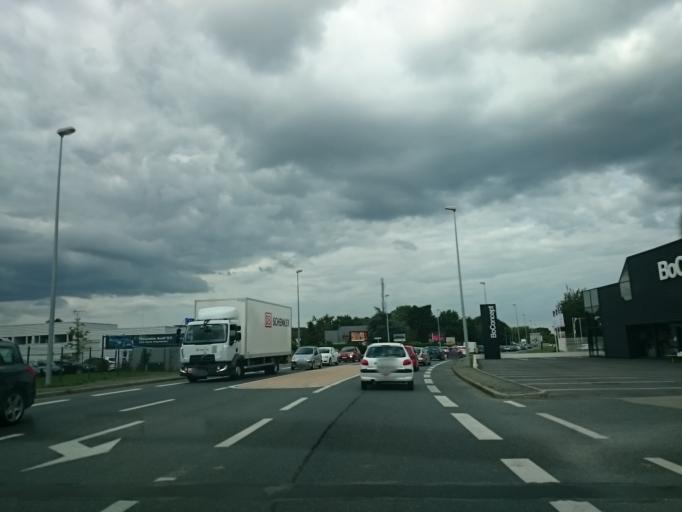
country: FR
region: Pays de la Loire
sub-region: Departement de la Loire-Atlantique
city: Orvault
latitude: 47.2560
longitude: -1.6280
